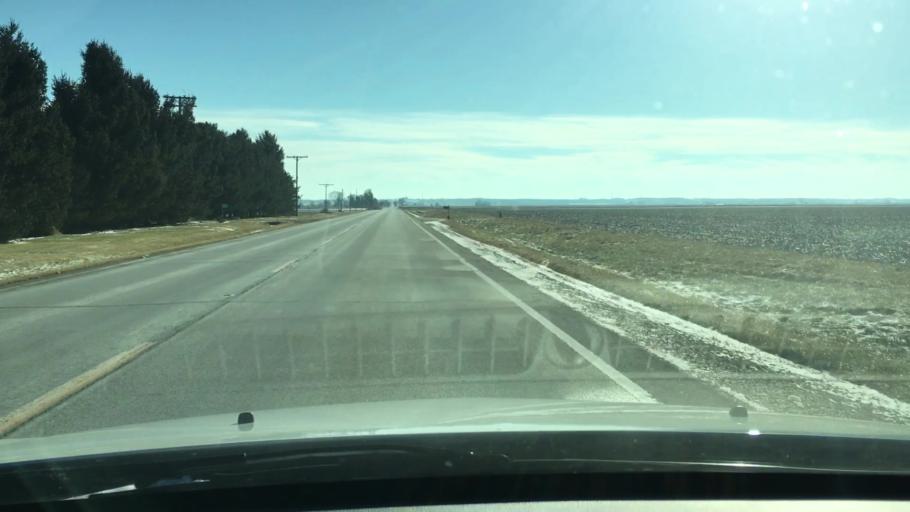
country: US
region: Illinois
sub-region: Ogle County
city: Rochelle
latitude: 41.7940
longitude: -89.0836
